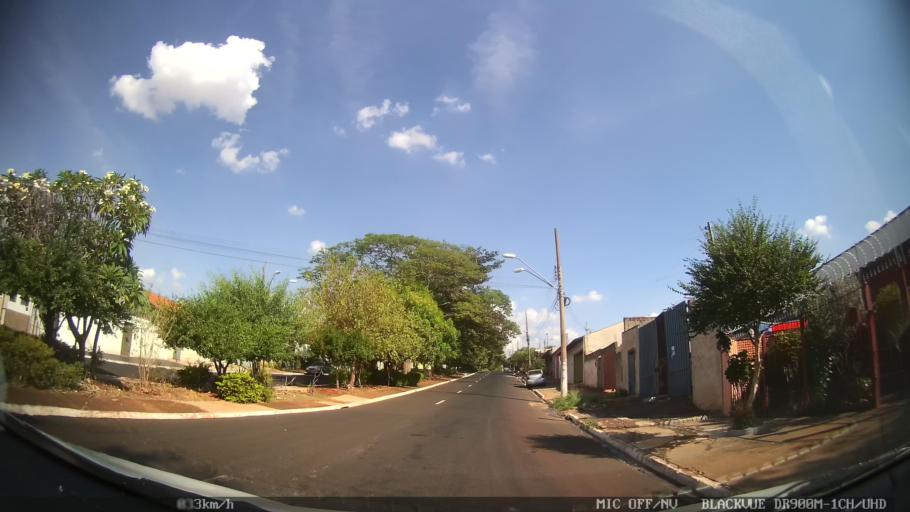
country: BR
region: Sao Paulo
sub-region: Ribeirao Preto
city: Ribeirao Preto
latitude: -21.1793
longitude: -47.8311
